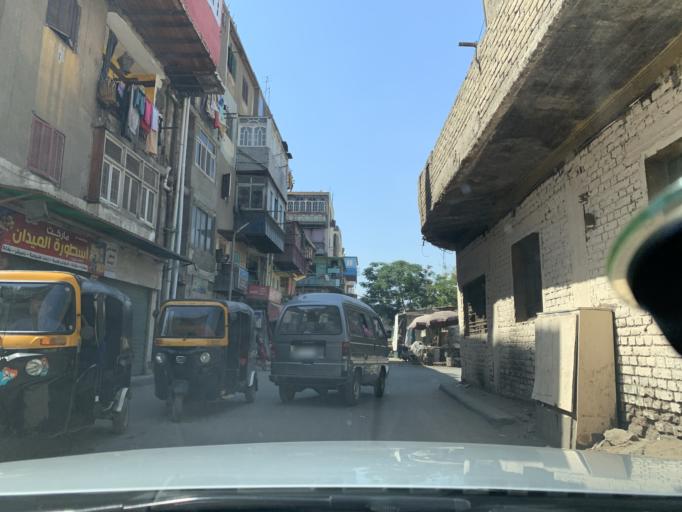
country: EG
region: Muhafazat al Qahirah
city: Cairo
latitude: 30.0768
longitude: 31.2581
